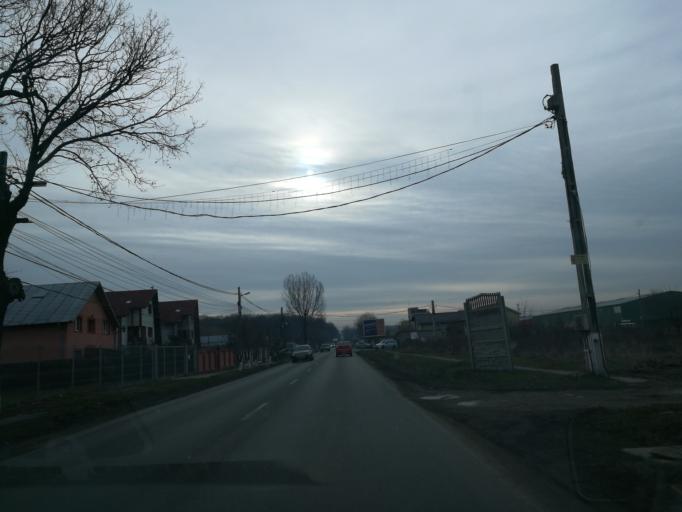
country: RO
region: Ilfov
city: Stefanestii de Jos
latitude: 44.5259
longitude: 26.1978
